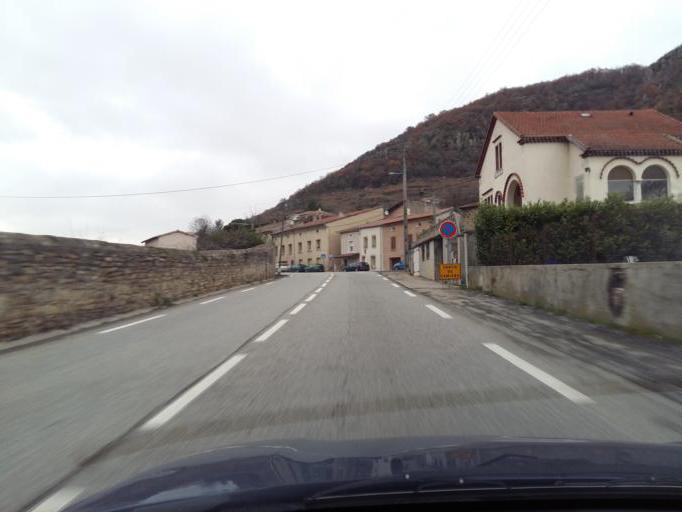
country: FR
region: Rhone-Alpes
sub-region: Departement de l'Ardeche
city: Andance
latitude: 45.2404
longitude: 4.7958
